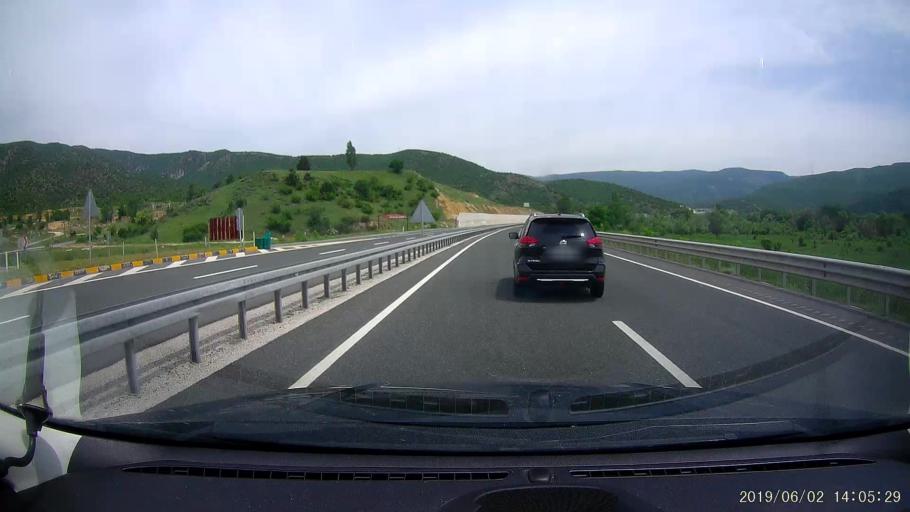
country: TR
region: Cankiri
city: Ilgaz
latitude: 40.9010
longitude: 33.6694
